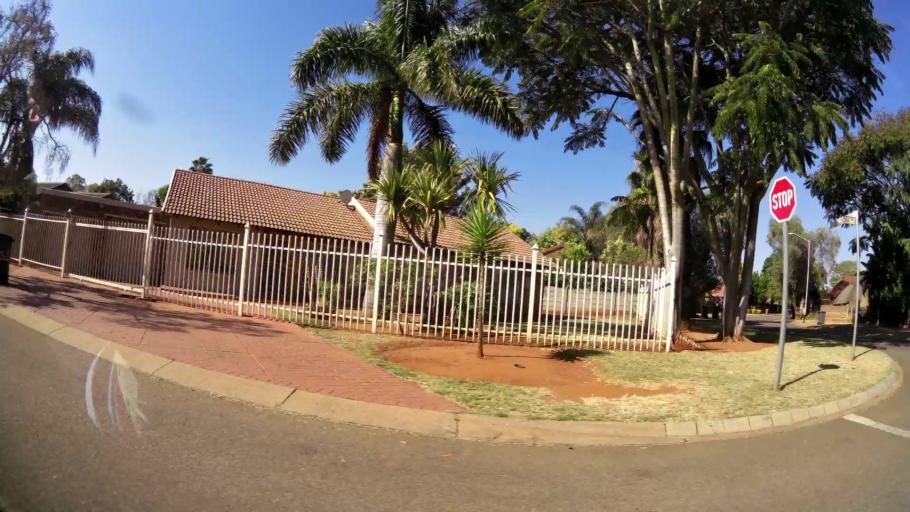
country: ZA
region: Gauteng
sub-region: City of Tshwane Metropolitan Municipality
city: Pretoria
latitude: -25.6526
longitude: 28.2555
